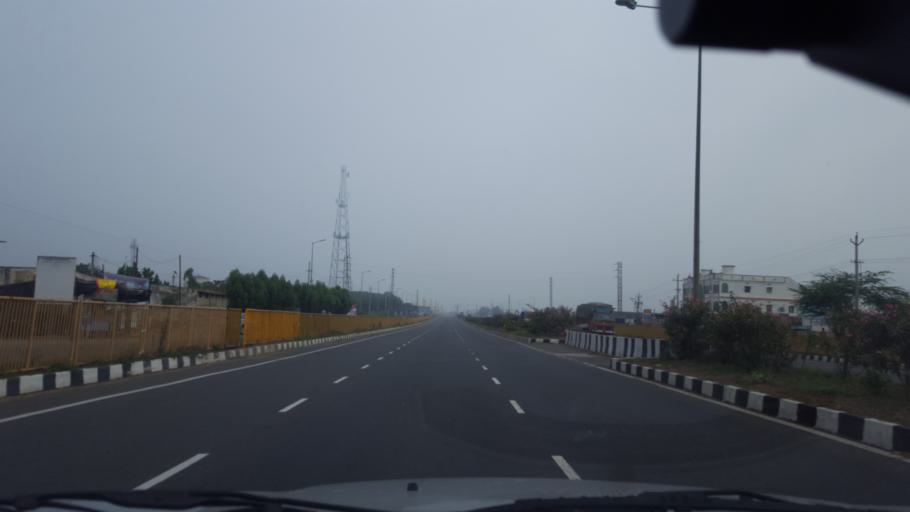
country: IN
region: Andhra Pradesh
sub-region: Prakasam
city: pedda nakkalapalem
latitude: 15.9727
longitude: 80.0968
